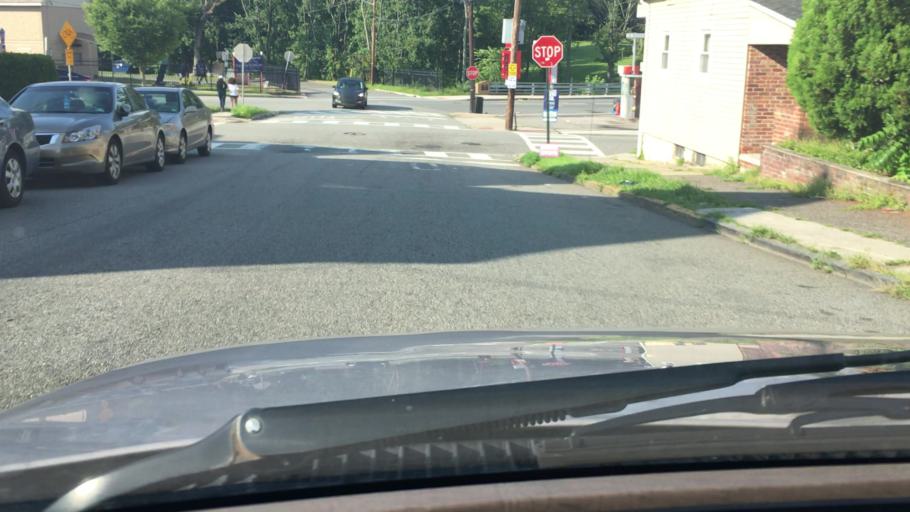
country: US
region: New Jersey
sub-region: Passaic County
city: Paterson
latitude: 40.9102
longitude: -74.1901
